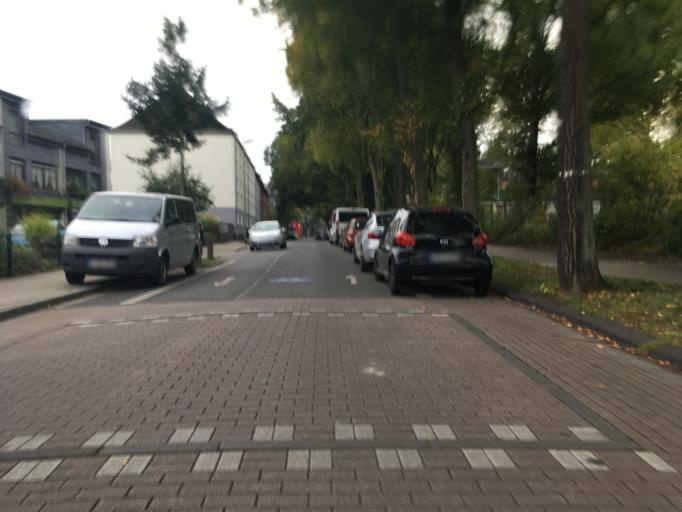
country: DE
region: North Rhine-Westphalia
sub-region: Regierungsbezirk Dusseldorf
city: Essen
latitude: 51.4815
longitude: 7.0083
